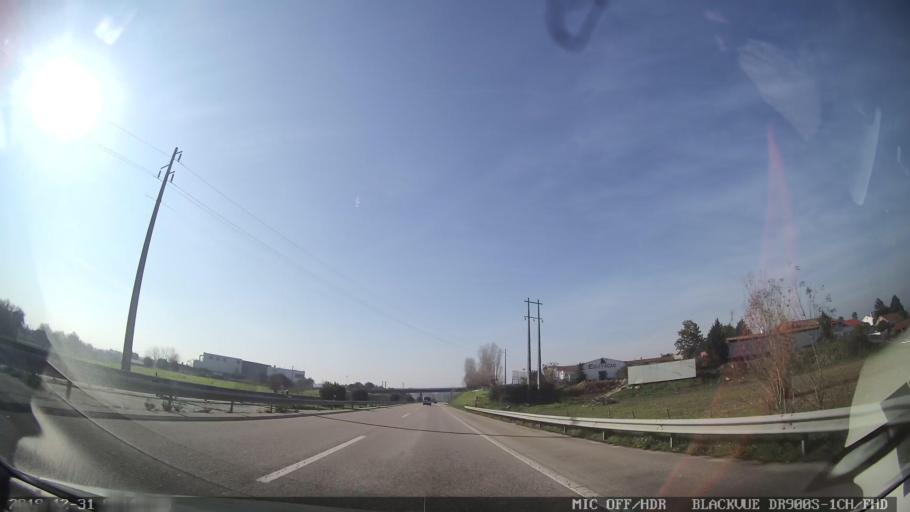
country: PT
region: Santarem
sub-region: Torres Novas
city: Torres Novas
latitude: 39.4677
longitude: -8.5218
